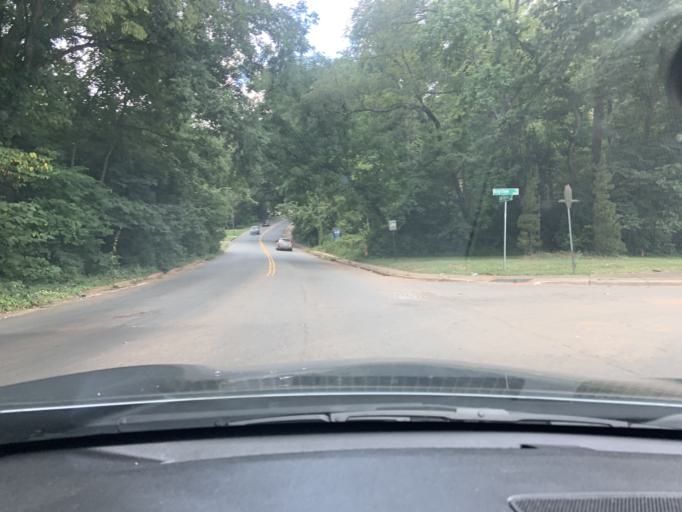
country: US
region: North Carolina
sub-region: Mecklenburg County
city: Charlotte
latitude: 35.2348
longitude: -80.8819
